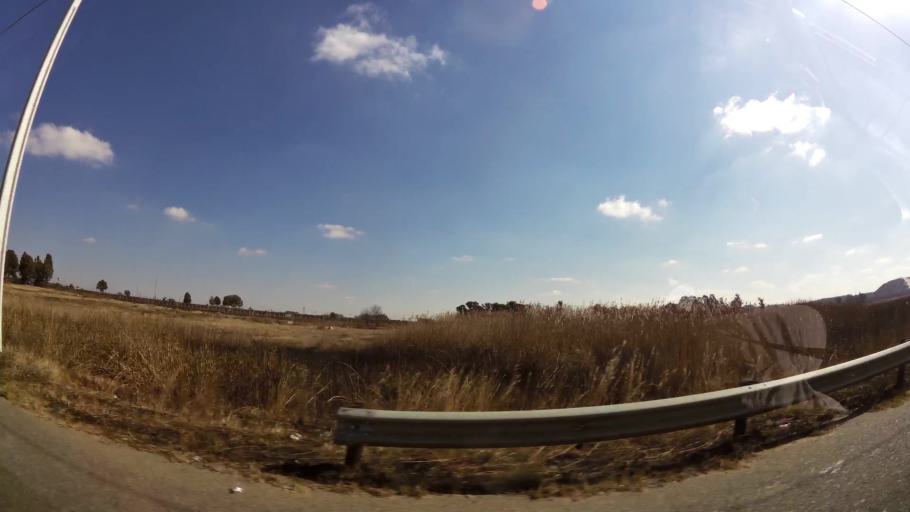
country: ZA
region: Gauteng
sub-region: West Rand District Municipality
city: Randfontein
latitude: -26.1532
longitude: 27.7627
